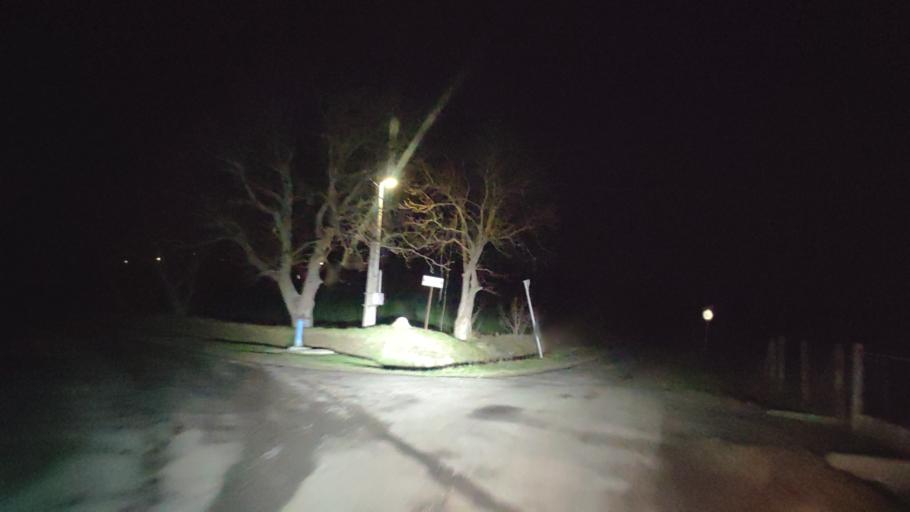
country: HU
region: Borsod-Abauj-Zemplen
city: Satoraljaujhely
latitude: 48.4887
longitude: 21.6096
